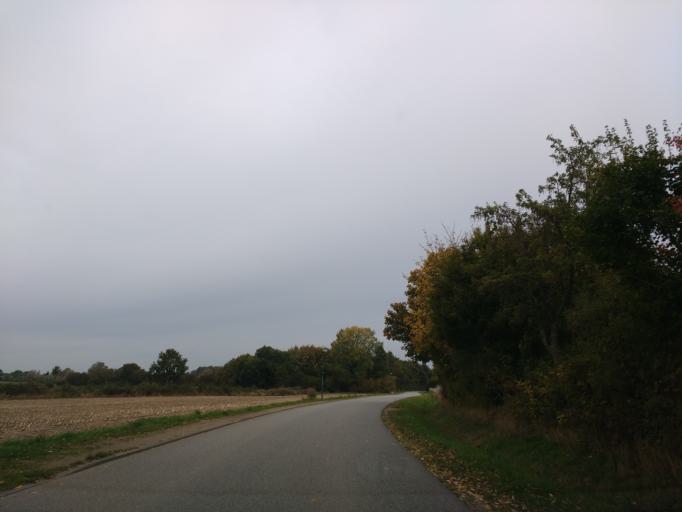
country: DE
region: Schleswig-Holstein
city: Grube
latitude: 54.1988
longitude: 11.0204
